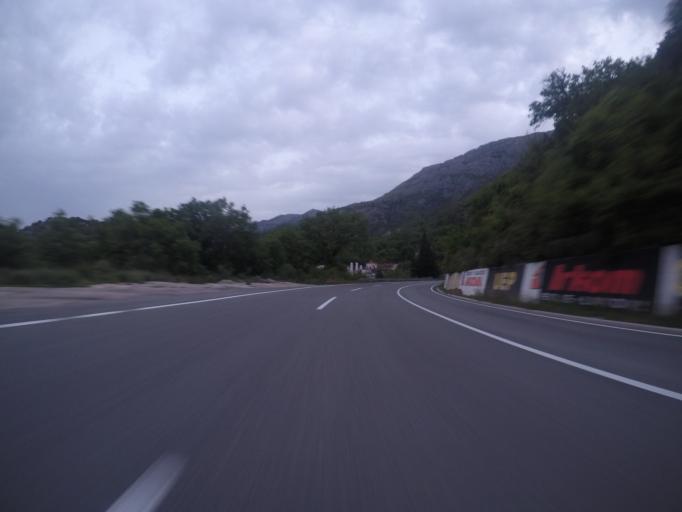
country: ME
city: Petrovac na Moru
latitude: 42.1945
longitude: 18.9832
